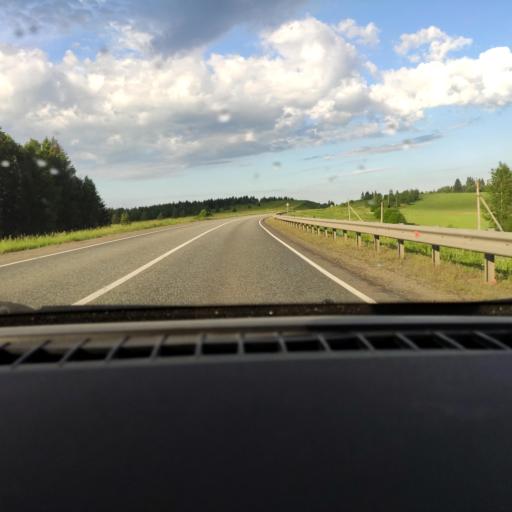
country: RU
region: Udmurtiya
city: Votkinsk
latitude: 57.2490
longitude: 54.2191
